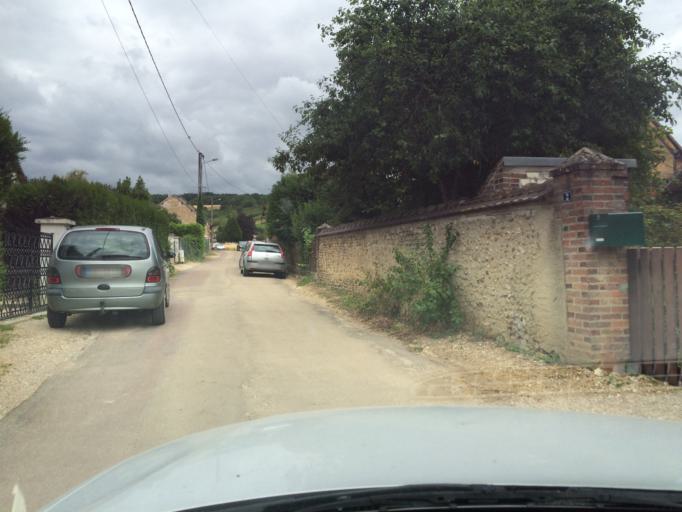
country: FR
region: Bourgogne
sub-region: Departement de l'Yonne
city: Cezy
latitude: 47.9397
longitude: 3.3480
